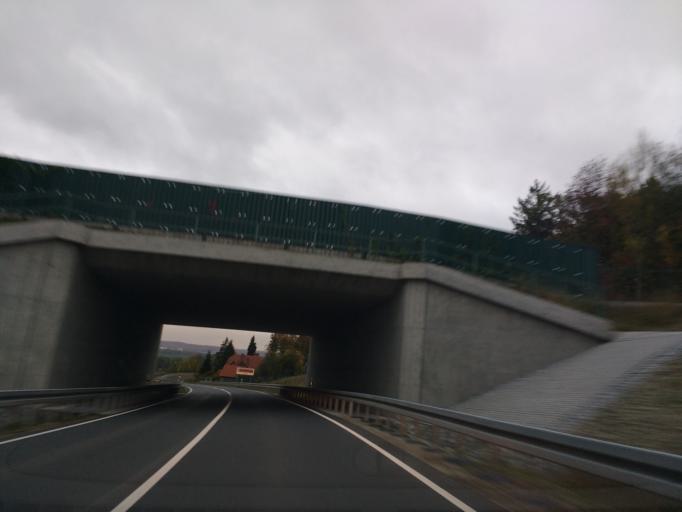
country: DE
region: Thuringia
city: Buhla
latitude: 51.4381
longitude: 10.4426
